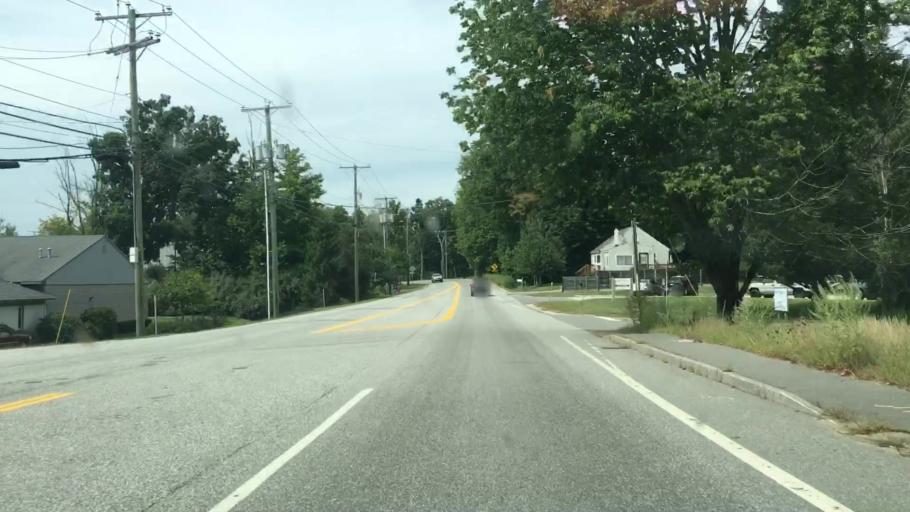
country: US
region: New Hampshire
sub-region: Strafford County
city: Dover
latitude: 43.1877
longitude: -70.8988
